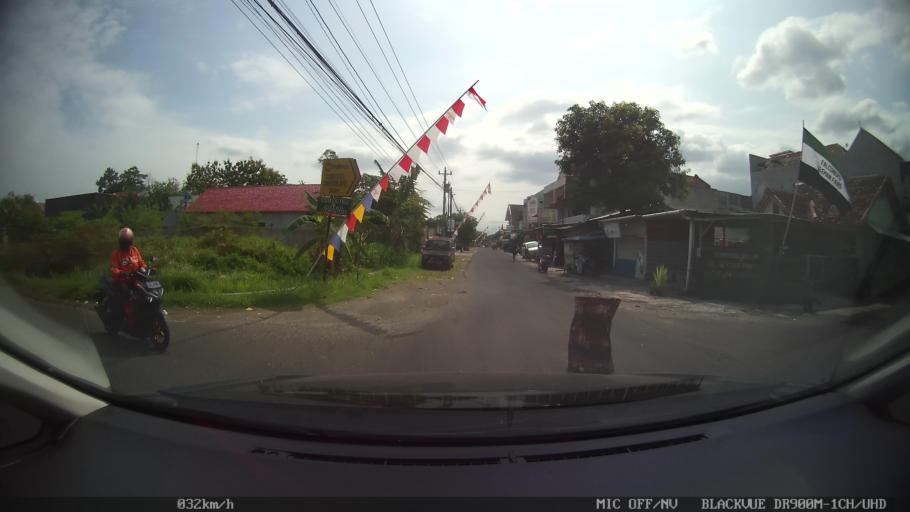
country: ID
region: Daerah Istimewa Yogyakarta
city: Depok
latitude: -7.7596
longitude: 110.4247
